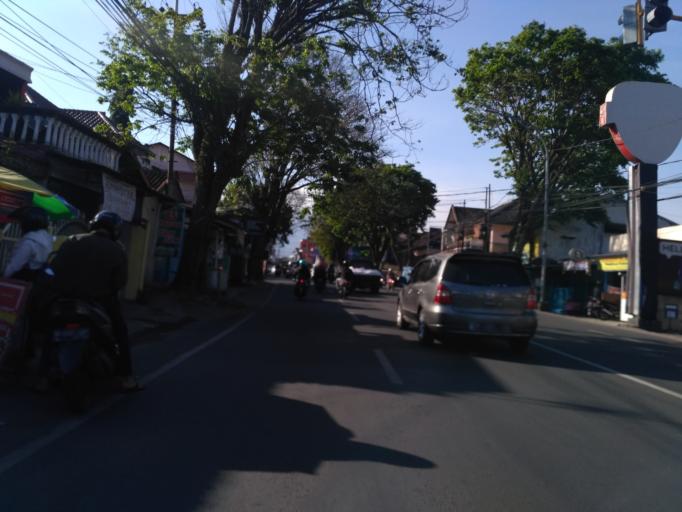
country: ID
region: East Java
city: Malang
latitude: -7.9291
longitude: 112.6030
